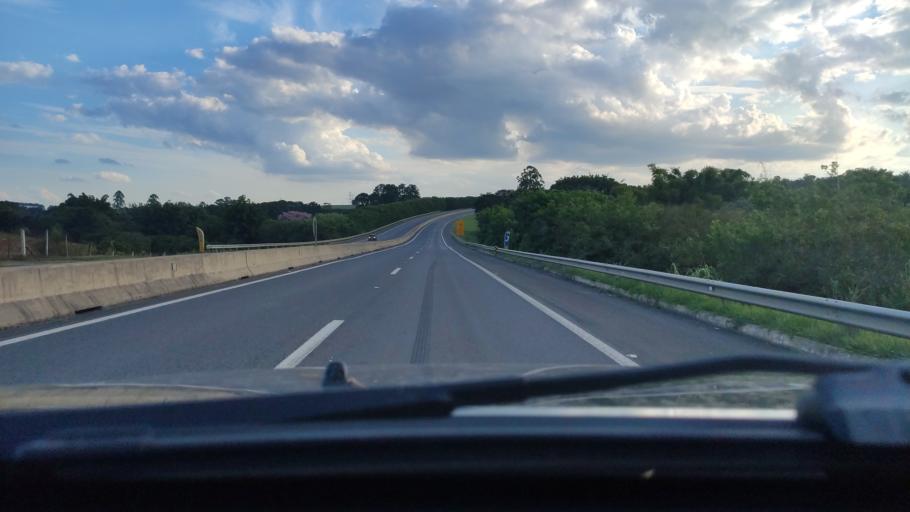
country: BR
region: Sao Paulo
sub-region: Mogi-Mirim
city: Mogi Mirim
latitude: -22.4463
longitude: -47.0558
